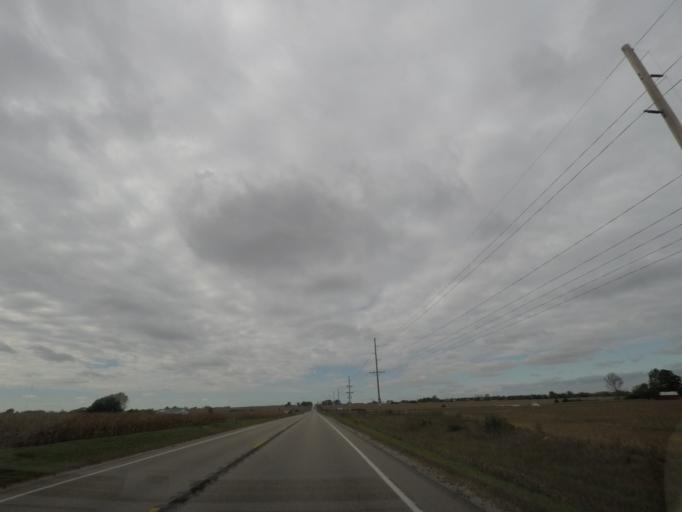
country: US
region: Iowa
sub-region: Story County
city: Huxley
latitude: 41.8777
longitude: -93.5276
